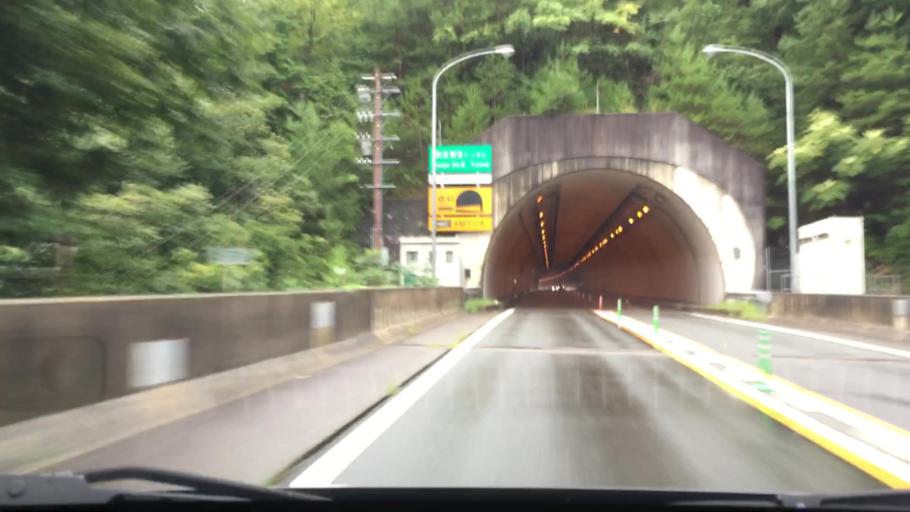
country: JP
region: Hyogo
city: Toyooka
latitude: 35.2755
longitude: 134.8142
